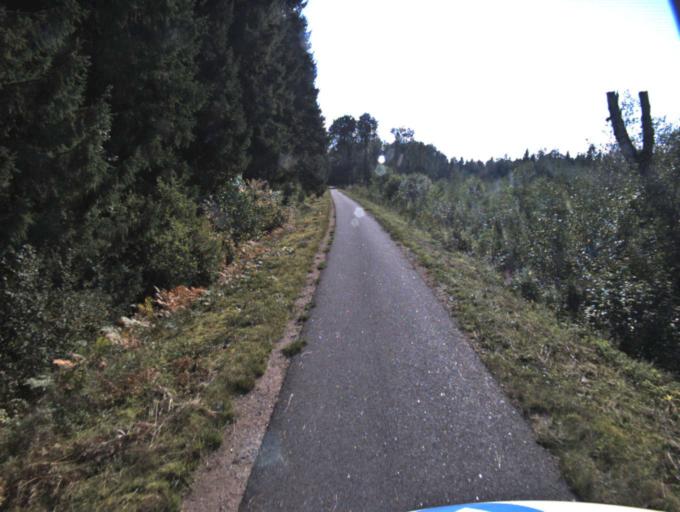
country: SE
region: Vaestra Goetaland
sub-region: Boras Kommun
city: Dalsjofors
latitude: 57.8142
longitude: 13.1404
